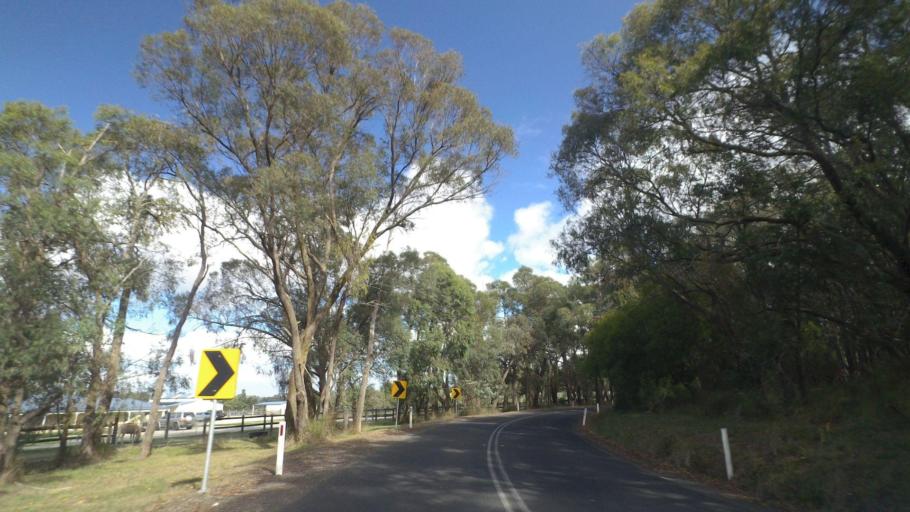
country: AU
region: Victoria
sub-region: Cardinia
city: Garfield
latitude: -38.0364
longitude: 145.6319
